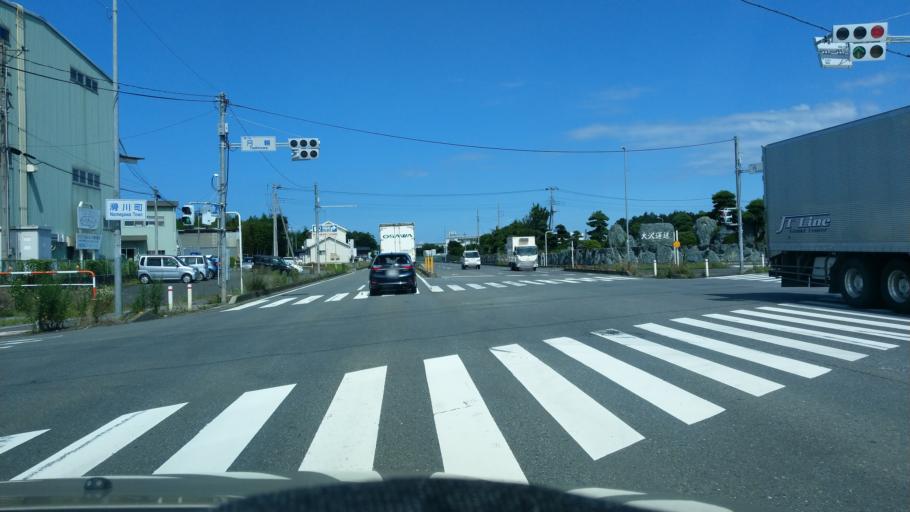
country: JP
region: Saitama
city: Sakado
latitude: 36.0377
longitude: 139.3556
